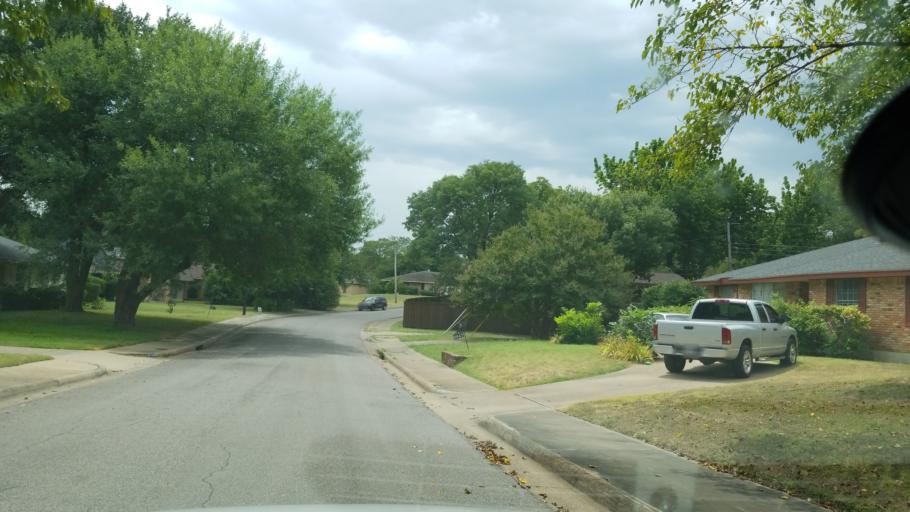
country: US
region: Texas
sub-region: Dallas County
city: Duncanville
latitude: 32.6637
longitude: -96.8356
